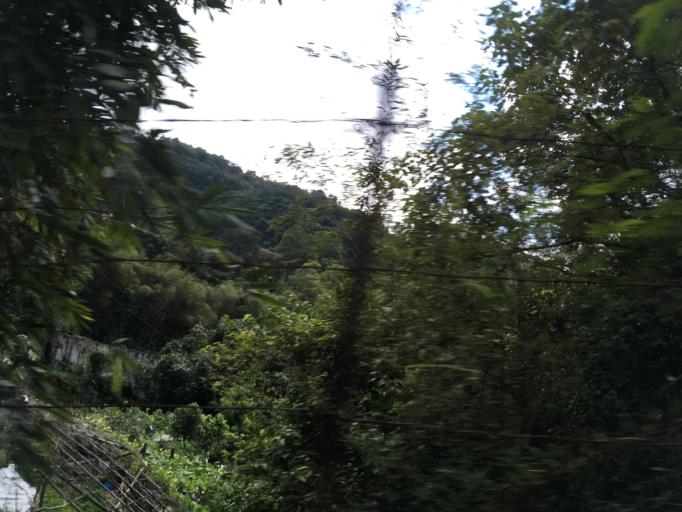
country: TW
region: Taipei
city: Taipei
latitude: 24.9491
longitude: 121.5579
